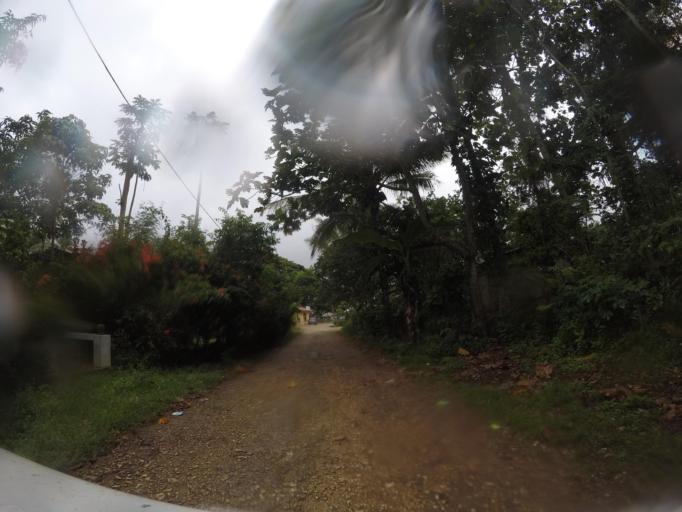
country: TL
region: Lautem
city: Lospalos
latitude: -8.5261
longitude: 126.9948
